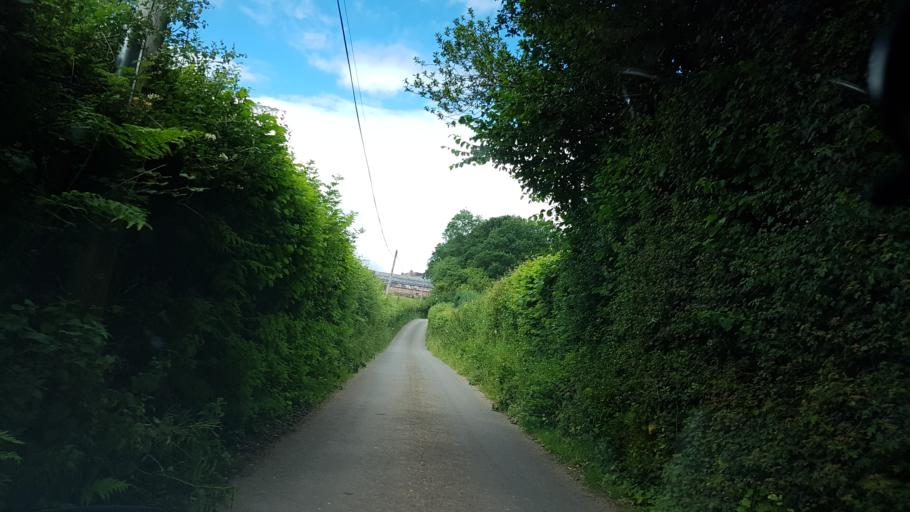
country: GB
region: Wales
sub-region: Monmouthshire
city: Llanarth
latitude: 51.8412
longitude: -2.8919
